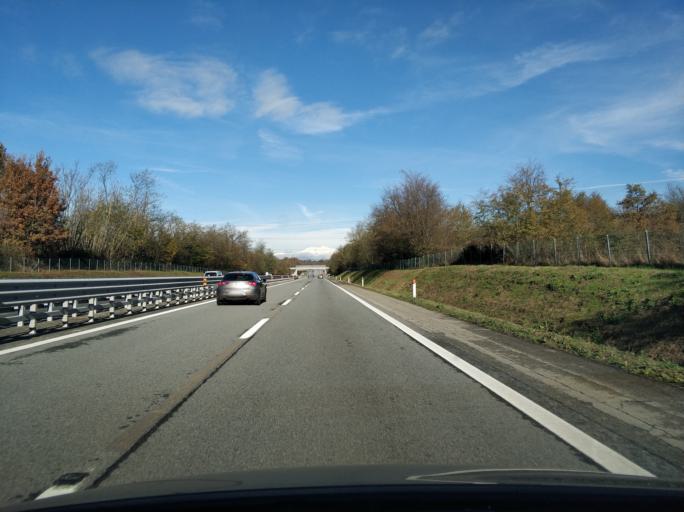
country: IT
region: Piedmont
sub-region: Provincia di Torino
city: Montalenghe
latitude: 45.3300
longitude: 7.8243
